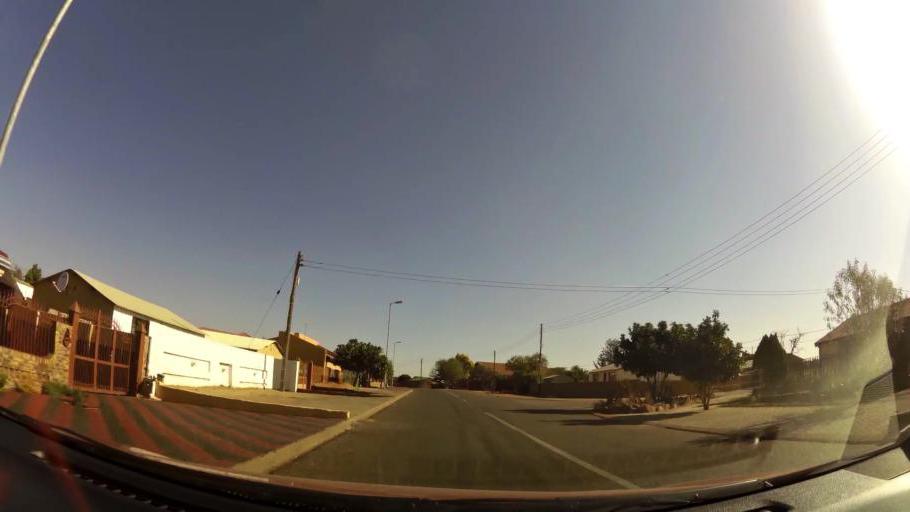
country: ZA
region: Gauteng
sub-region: City of Tshwane Metropolitan Municipality
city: Mabopane
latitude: -25.5295
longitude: 28.1010
